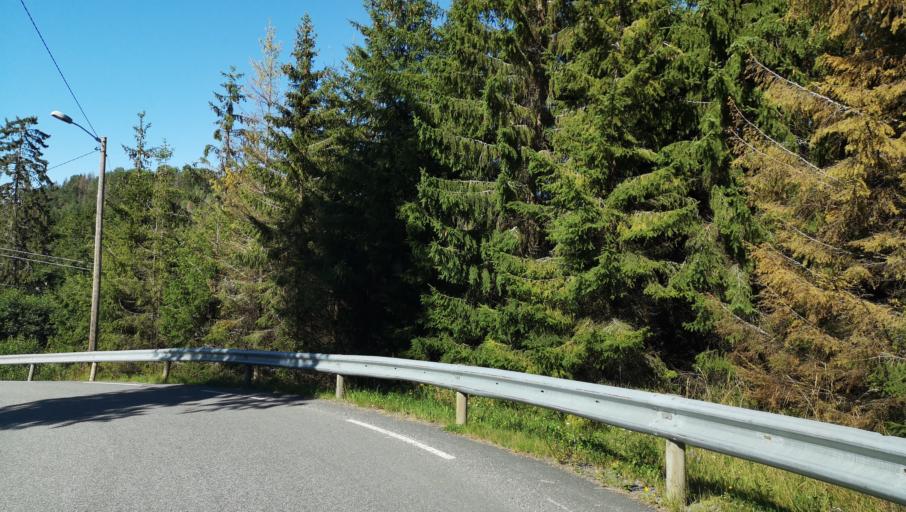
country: NO
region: Ostfold
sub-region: Hobol
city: Tomter
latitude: 59.6563
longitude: 11.0051
